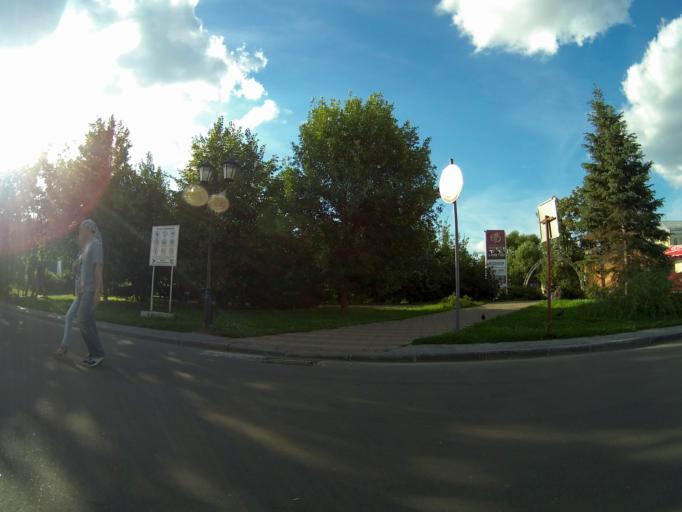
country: RU
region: Vladimir
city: Vladimir
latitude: 56.1293
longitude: 40.4021
